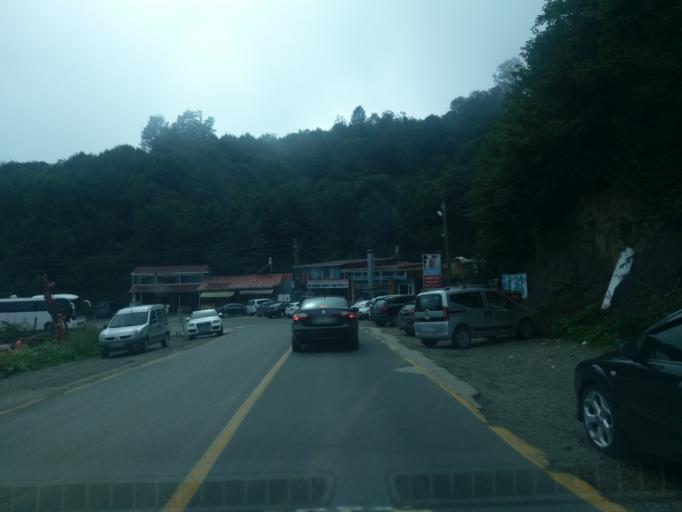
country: TR
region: Ordu
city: Gurgentepe
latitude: 40.8526
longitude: 37.6603
